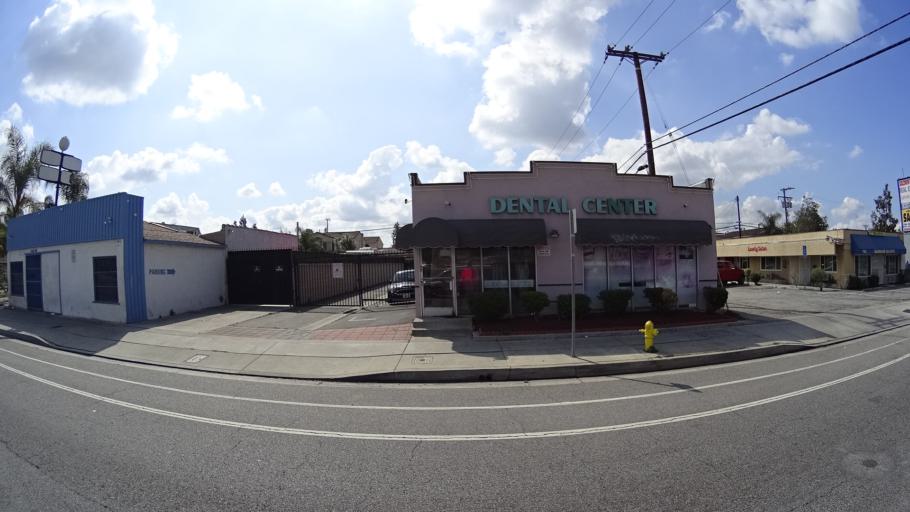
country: US
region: California
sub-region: Los Angeles County
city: Baldwin Park
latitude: 34.0847
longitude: -117.9674
